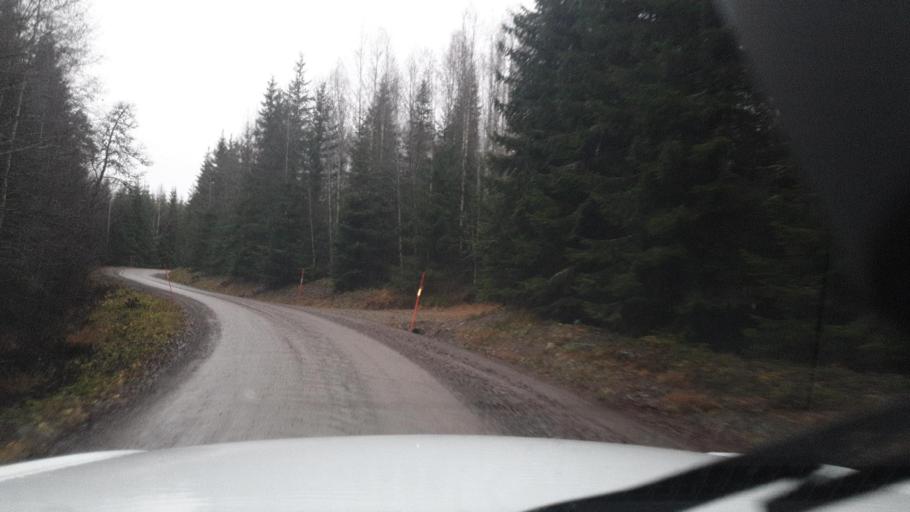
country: SE
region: Vaermland
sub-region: Arvika Kommun
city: Arvika
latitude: 59.9532
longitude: 12.6590
